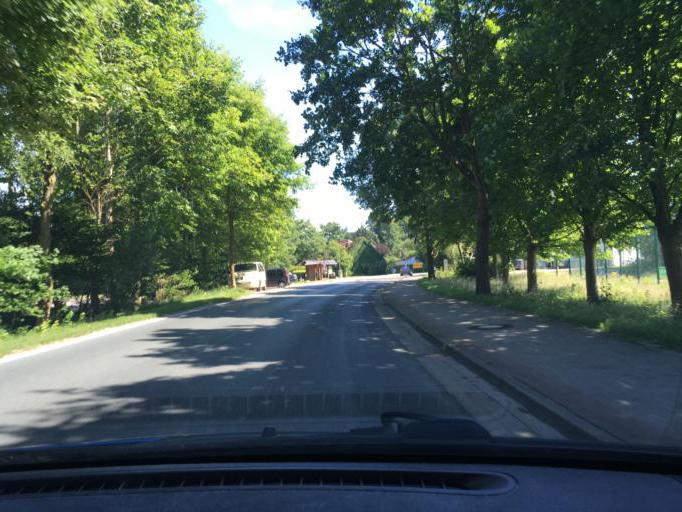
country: DE
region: Lower Saxony
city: Buchholz in der Nordheide
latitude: 53.3695
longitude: 9.9089
